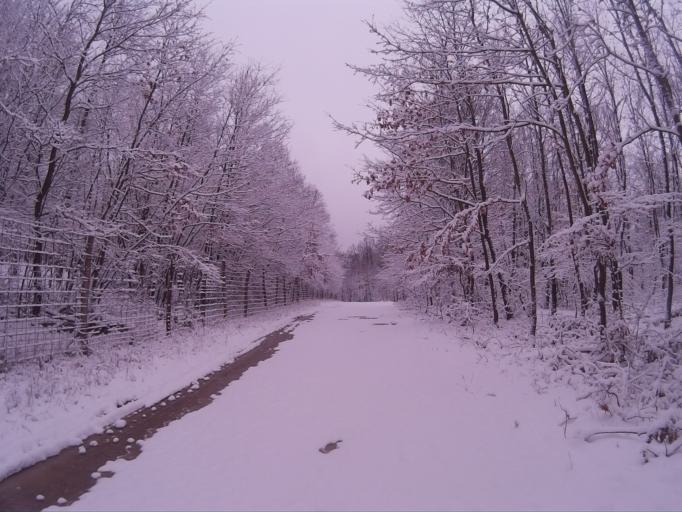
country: HU
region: Komarom-Esztergom
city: Tarjan
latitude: 47.5590
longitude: 18.5285
